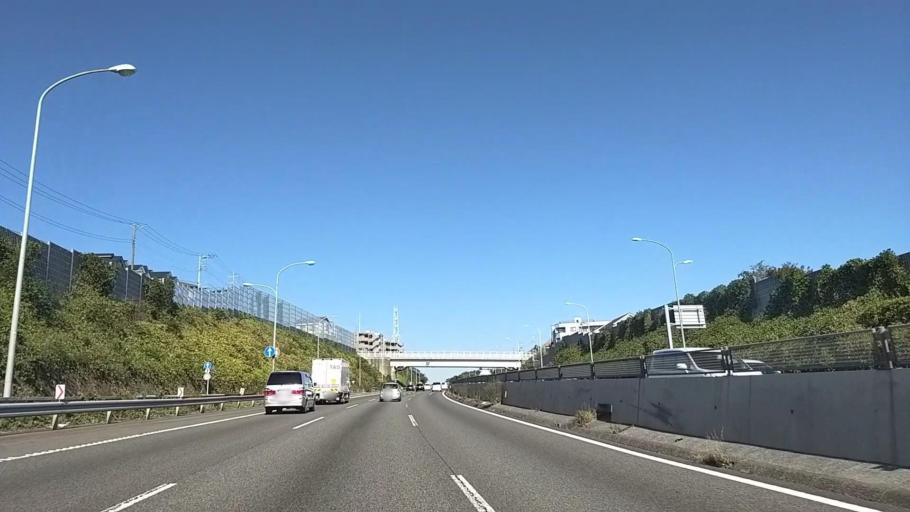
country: JP
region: Kanagawa
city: Minami-rinkan
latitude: 35.4683
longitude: 139.5340
